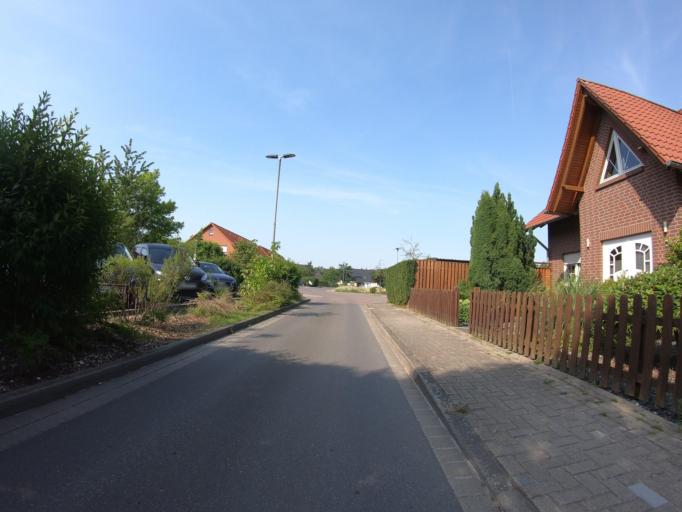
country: DE
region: Lower Saxony
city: Wagenhoff
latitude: 52.4992
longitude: 10.5147
